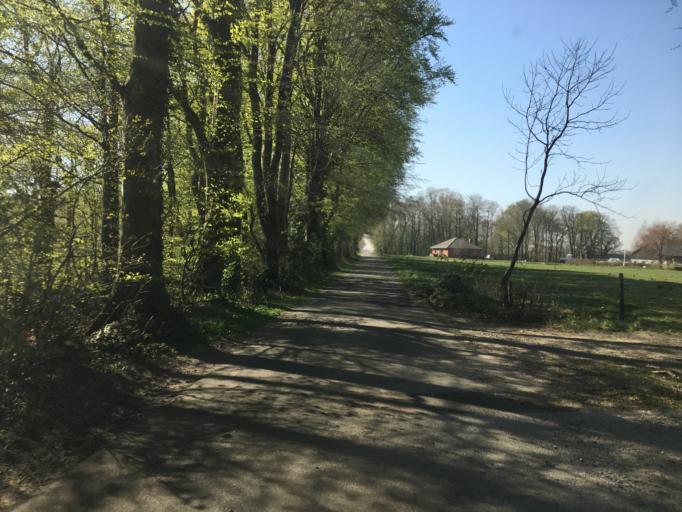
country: DK
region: South Denmark
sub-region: Aabenraa Kommune
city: Rodekro
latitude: 55.1051
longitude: 9.2374
